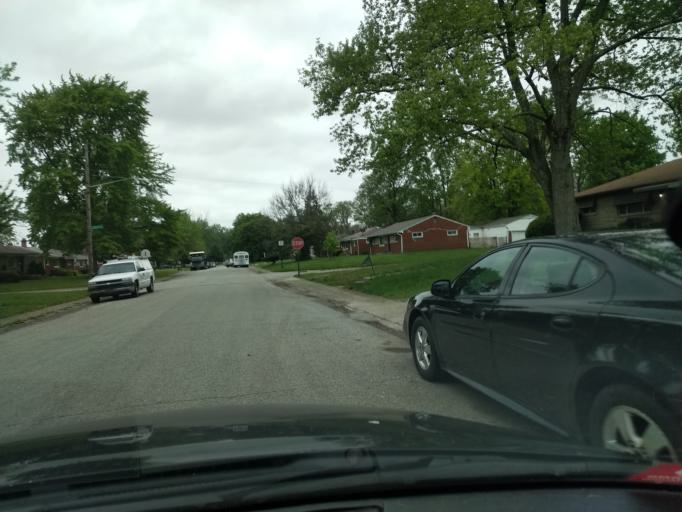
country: US
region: Indiana
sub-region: Marion County
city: Lawrence
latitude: 39.8279
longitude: -86.0662
